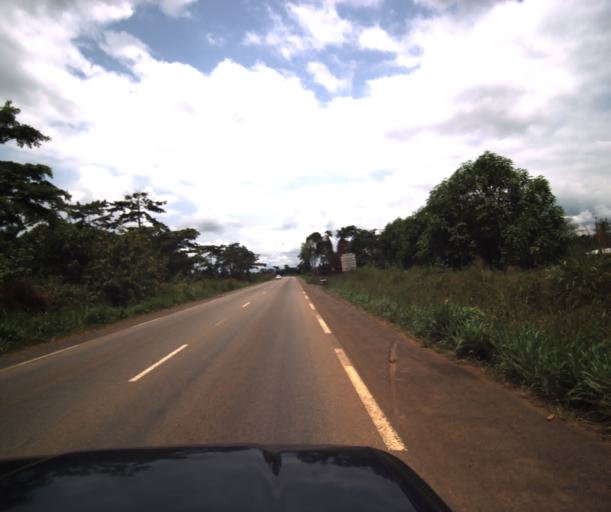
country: CM
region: Centre
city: Eseka
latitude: 3.8572
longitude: 10.9375
